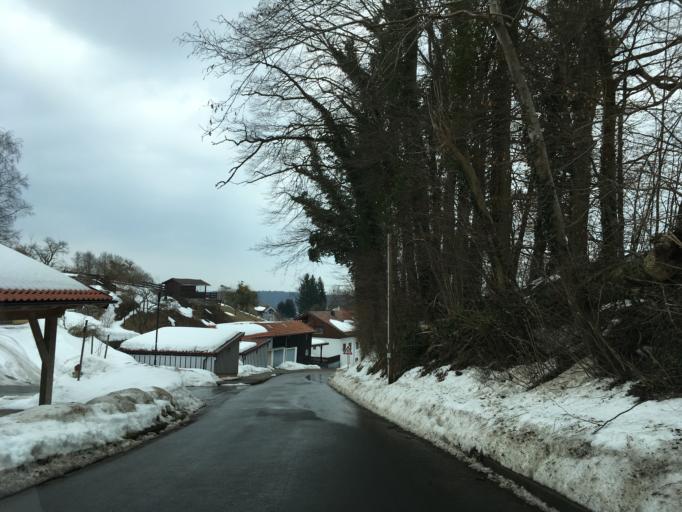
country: DE
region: Bavaria
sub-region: Upper Bavaria
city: Rimsting
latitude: 47.9111
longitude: 12.3325
